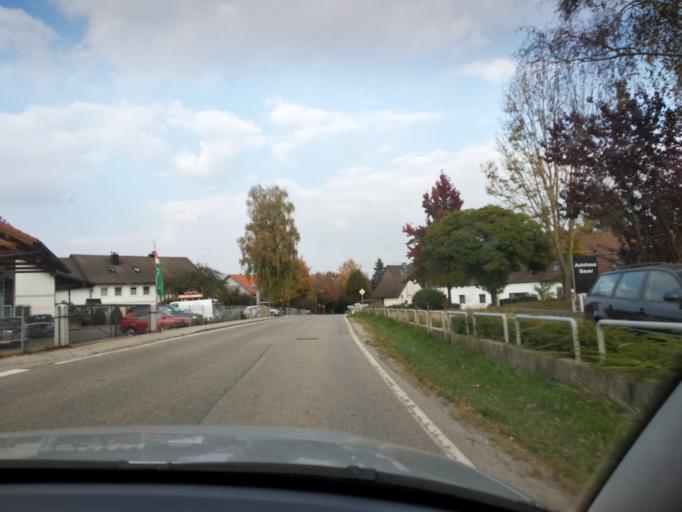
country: DE
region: Bavaria
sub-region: Upper Bavaria
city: Ottenhofen
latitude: 48.2126
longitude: 11.8779
